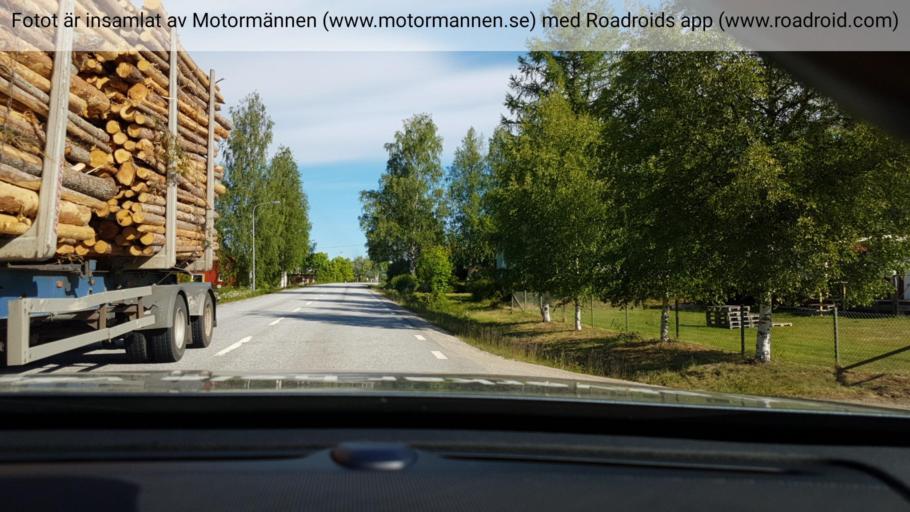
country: SE
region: Vaesterbotten
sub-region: Vindelns Kommun
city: Vindeln
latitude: 64.1610
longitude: 19.5013
